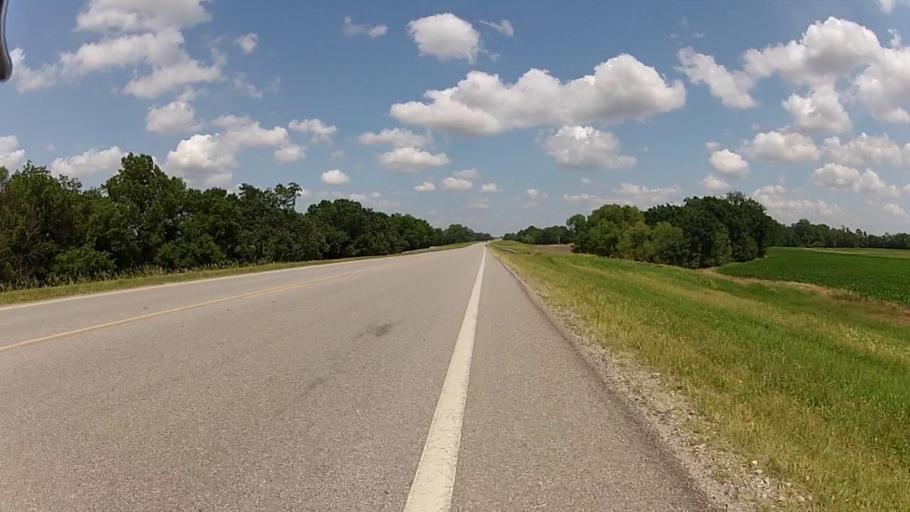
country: US
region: Kansas
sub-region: Labette County
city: Altamont
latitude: 37.1936
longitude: -95.2080
